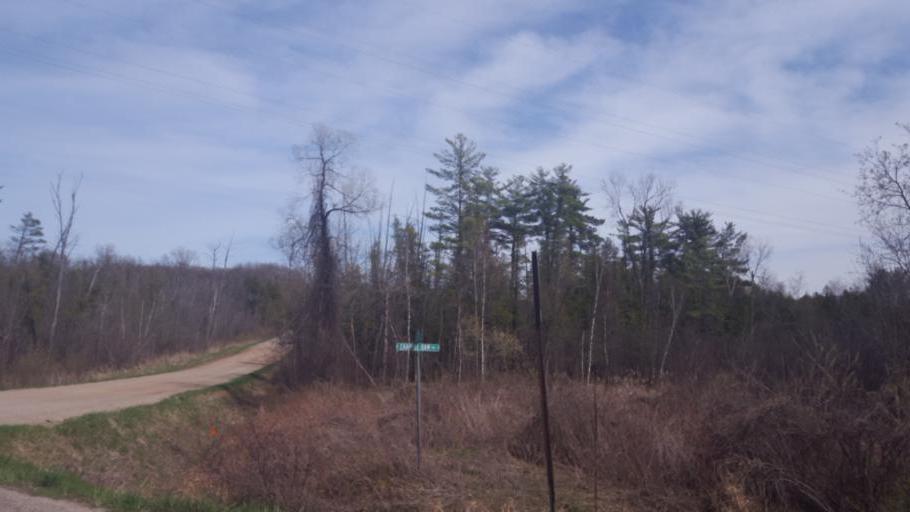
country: US
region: Michigan
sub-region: Gladwin County
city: Gladwin
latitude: 44.0165
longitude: -84.5247
